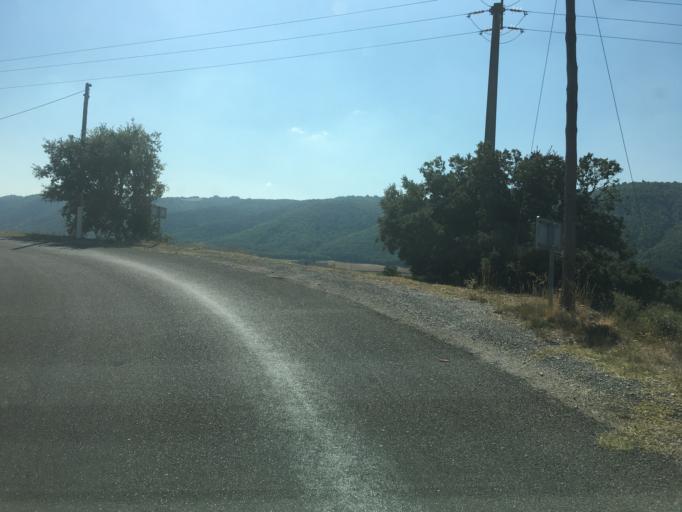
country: FR
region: Provence-Alpes-Cote d'Azur
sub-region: Departement des Alpes-de-Haute-Provence
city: Oraison
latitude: 43.8885
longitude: 5.9463
